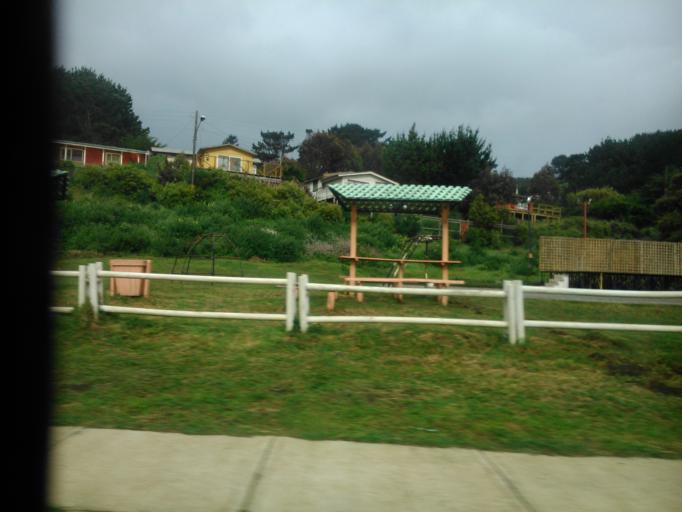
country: CL
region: Araucania
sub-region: Provincia de Cautin
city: Carahue
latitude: -38.8118
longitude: -73.3989
